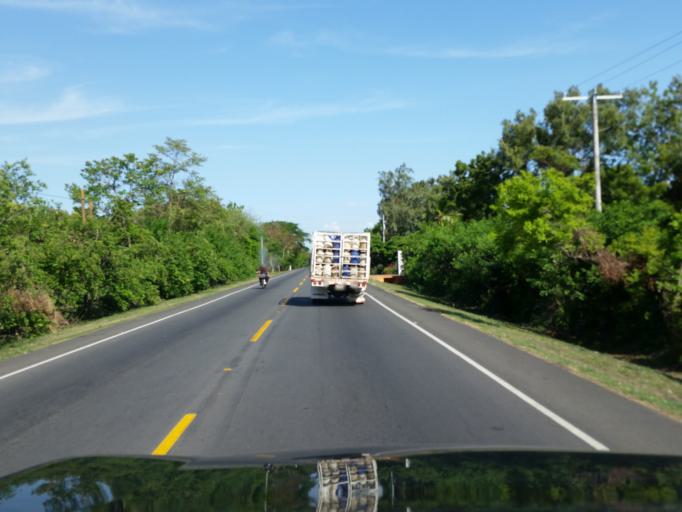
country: NI
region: Leon
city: Leon
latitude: 12.3942
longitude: -86.8486
